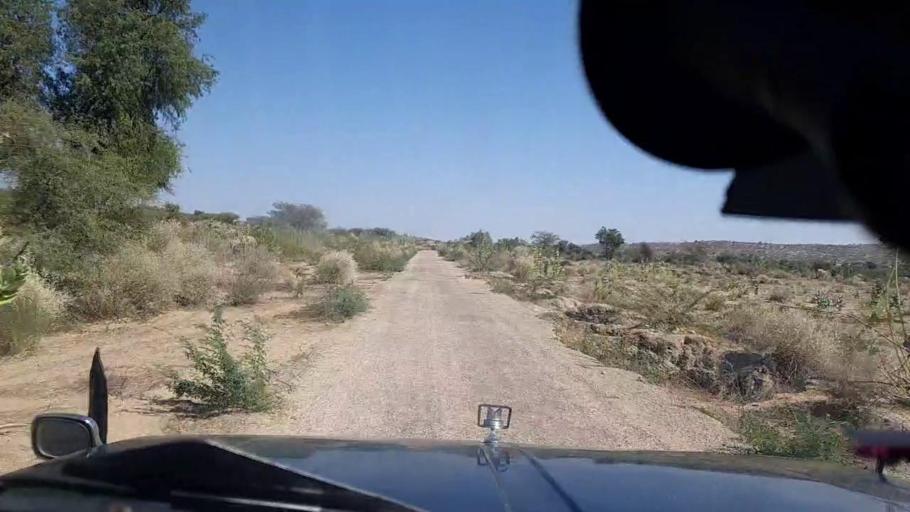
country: PK
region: Sindh
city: Diplo
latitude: 24.4232
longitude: 69.6740
